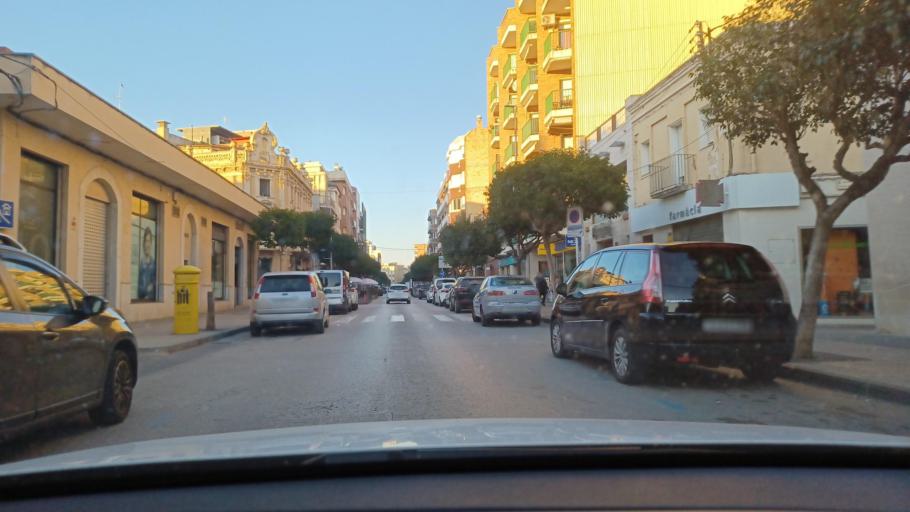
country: ES
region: Catalonia
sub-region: Provincia de Tarragona
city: Amposta
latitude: 40.7087
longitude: 0.5798
